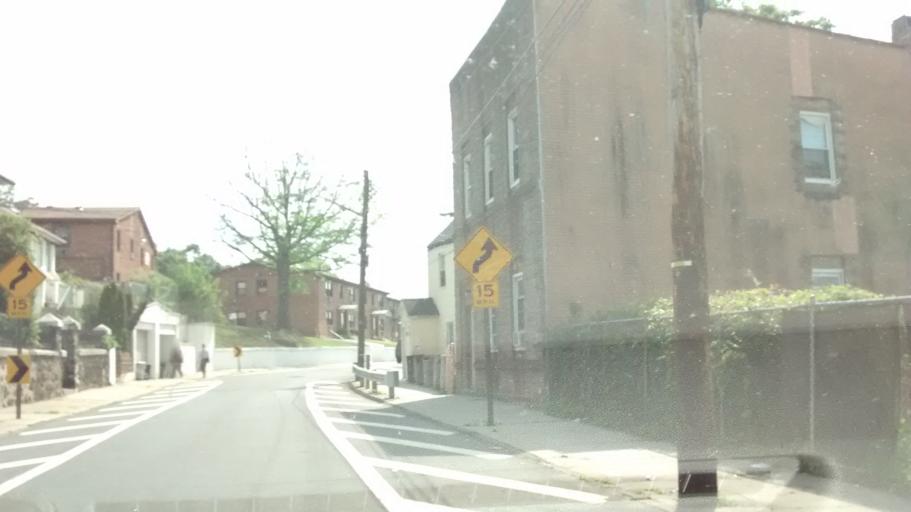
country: US
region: New Jersey
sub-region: Hudson County
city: Bayonne
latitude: 40.6272
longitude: -74.0831
